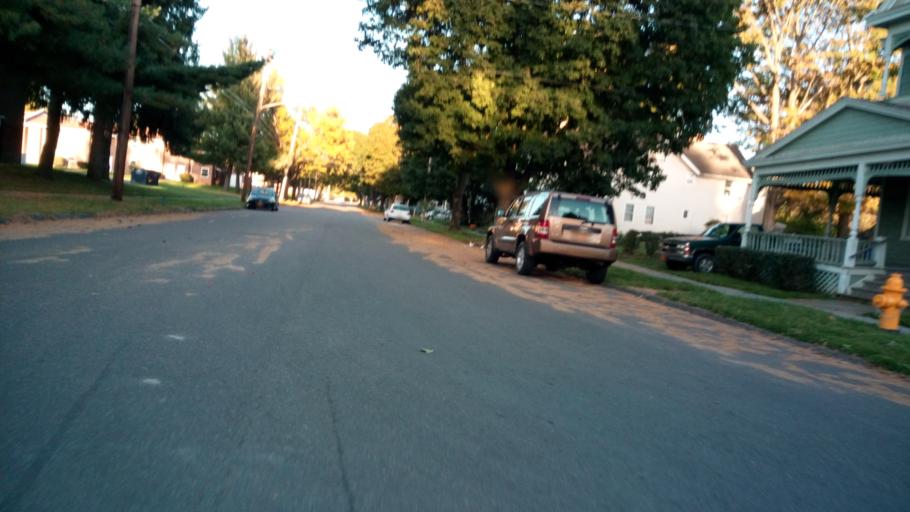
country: US
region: New York
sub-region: Chemung County
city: Elmira
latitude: 42.0838
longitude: -76.8093
